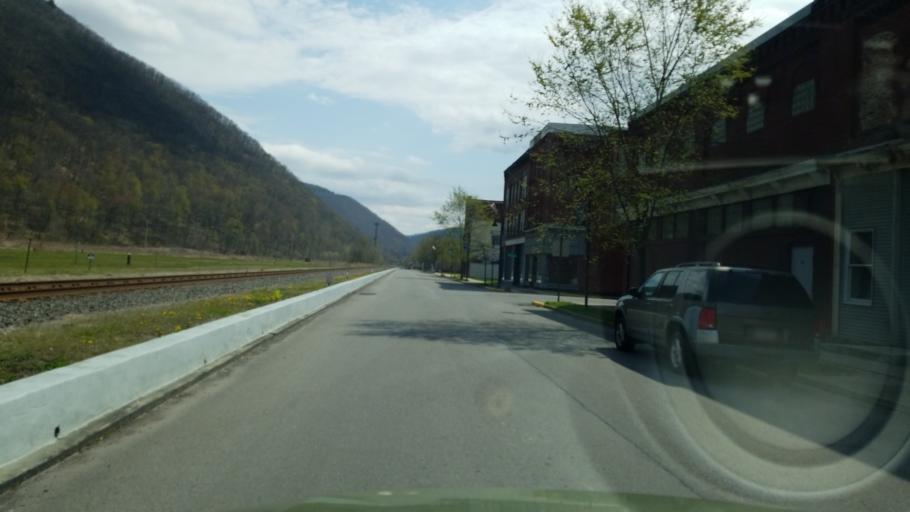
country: US
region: Pennsylvania
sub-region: Clinton County
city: Renovo
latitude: 41.3270
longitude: -77.7555
